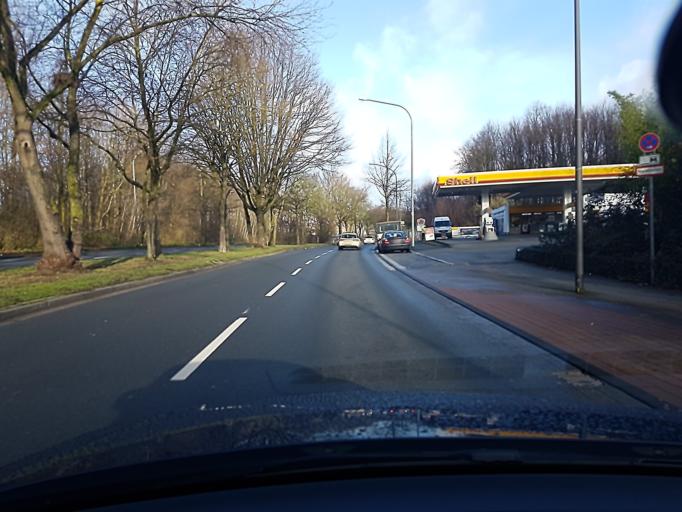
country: DE
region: North Rhine-Westphalia
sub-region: Regierungsbezirk Dusseldorf
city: Essen
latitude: 51.4705
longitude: 7.0068
